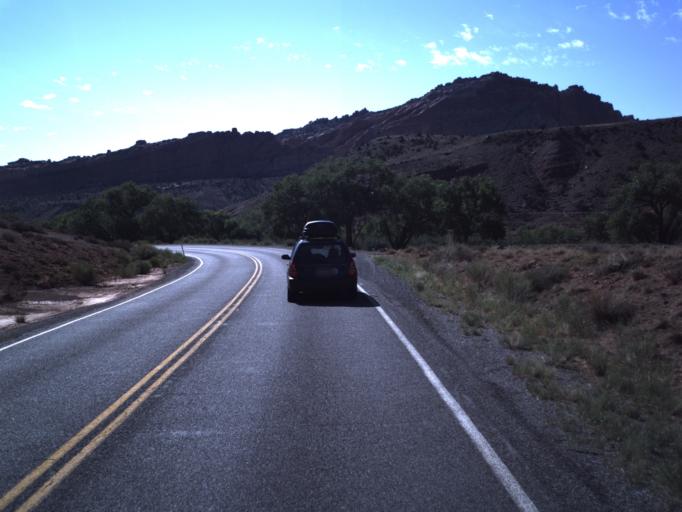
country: US
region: Utah
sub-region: Wayne County
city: Loa
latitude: 38.2905
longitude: -111.2572
